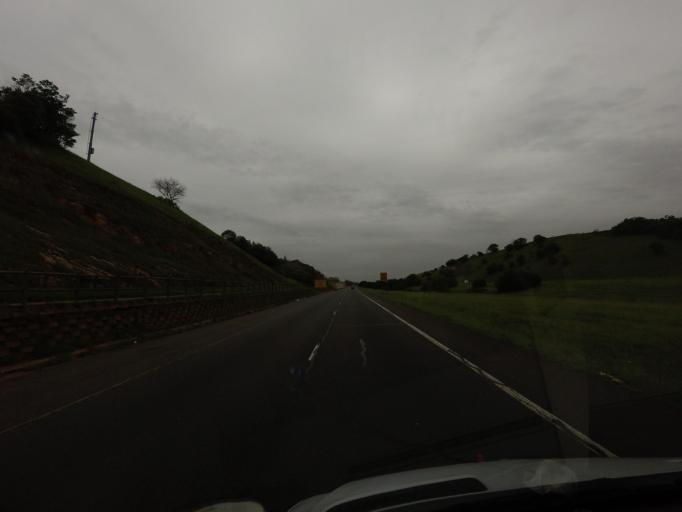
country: ZA
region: KwaZulu-Natal
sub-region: eThekwini Metropolitan Municipality
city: Durban
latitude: -29.7051
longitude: 31.0689
